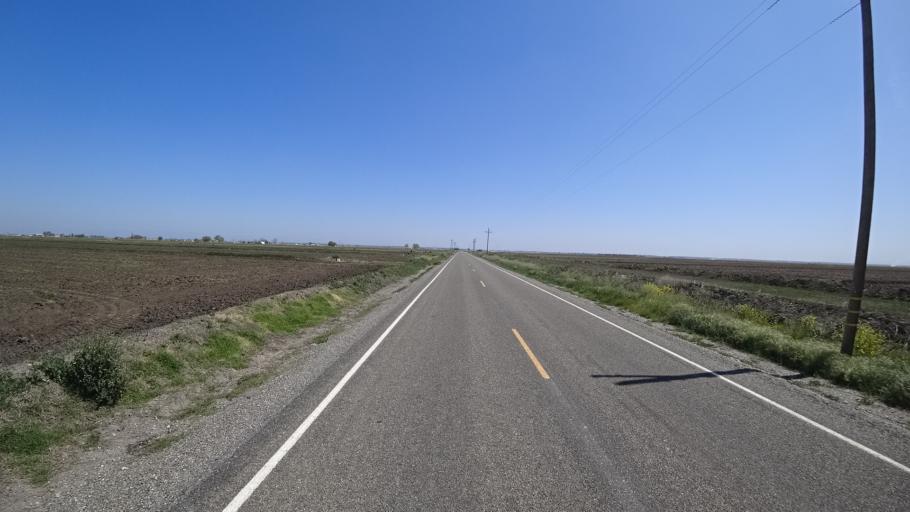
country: US
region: California
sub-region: Glenn County
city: Willows
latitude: 39.5582
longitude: -122.0773
